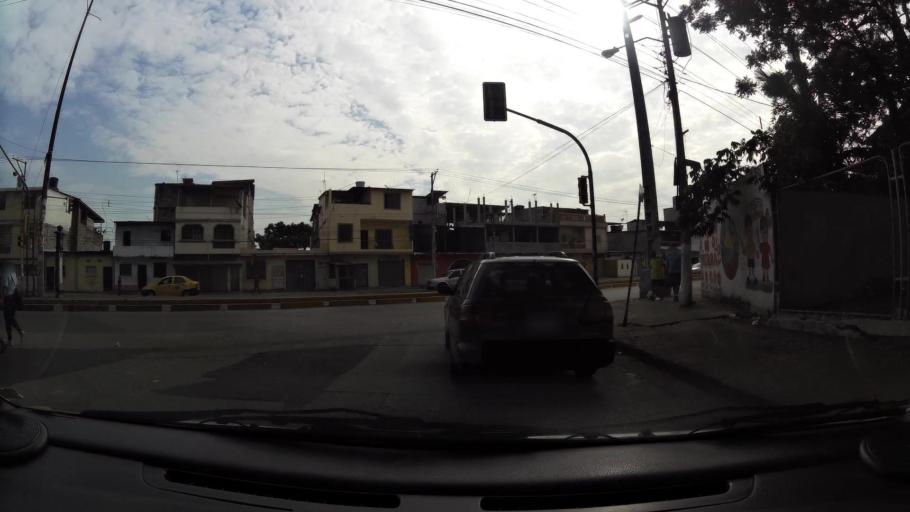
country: EC
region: Guayas
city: Guayaquil
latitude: -2.2511
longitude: -79.8855
